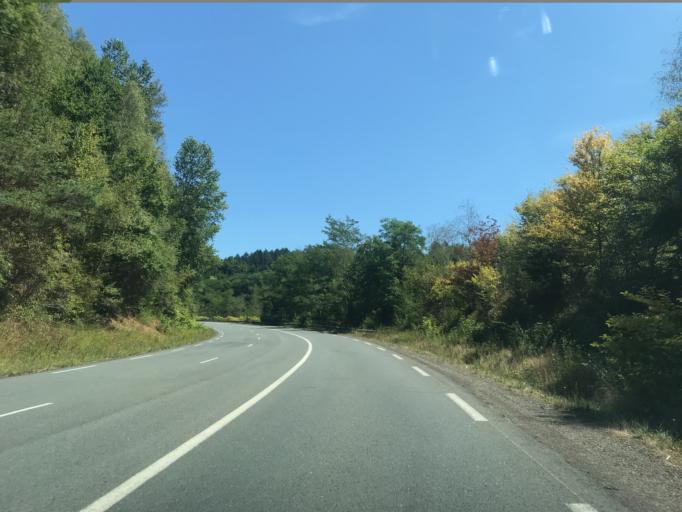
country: FR
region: Limousin
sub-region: Departement de la Correze
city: Chameyrat
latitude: 45.2323
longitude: 1.7246
